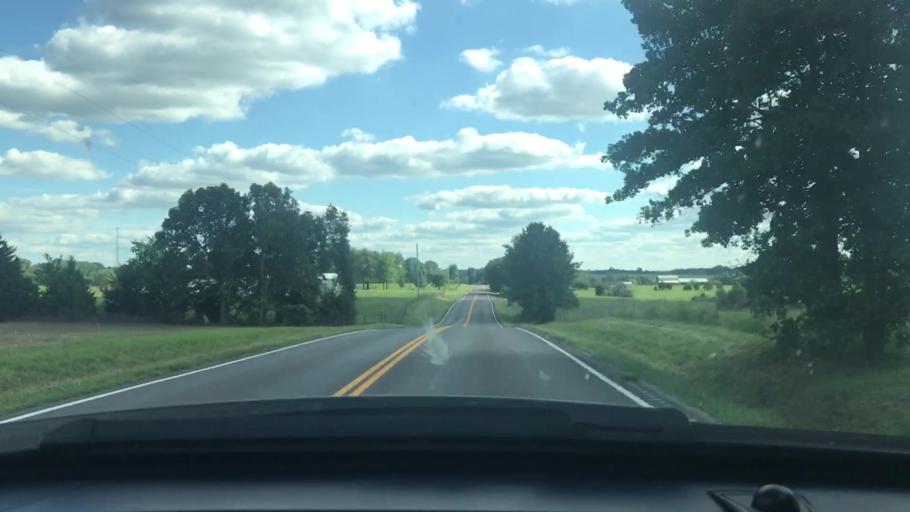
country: US
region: Missouri
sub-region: Wright County
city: Mountain Grove
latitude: 37.2621
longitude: -92.3081
